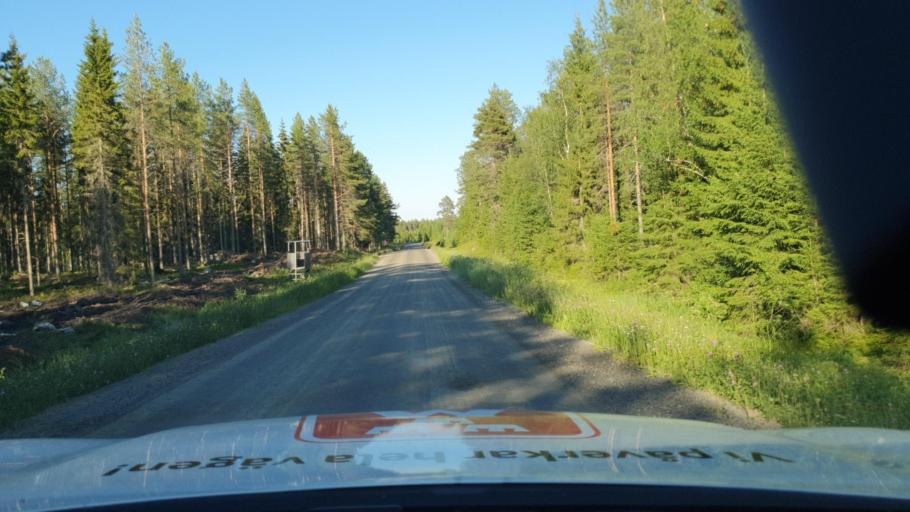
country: SE
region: Vaesterbotten
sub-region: Skelleftea Kommun
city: Burea
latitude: 64.5086
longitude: 21.3269
